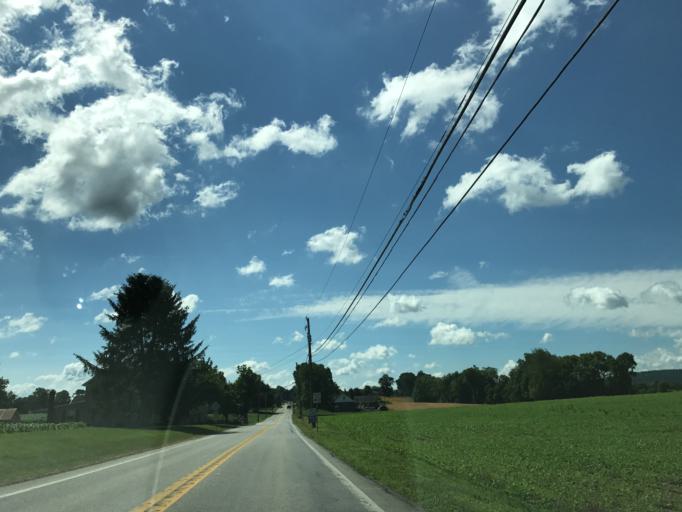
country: US
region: Pennsylvania
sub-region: Lancaster County
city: Maytown
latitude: 40.0841
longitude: -76.5905
